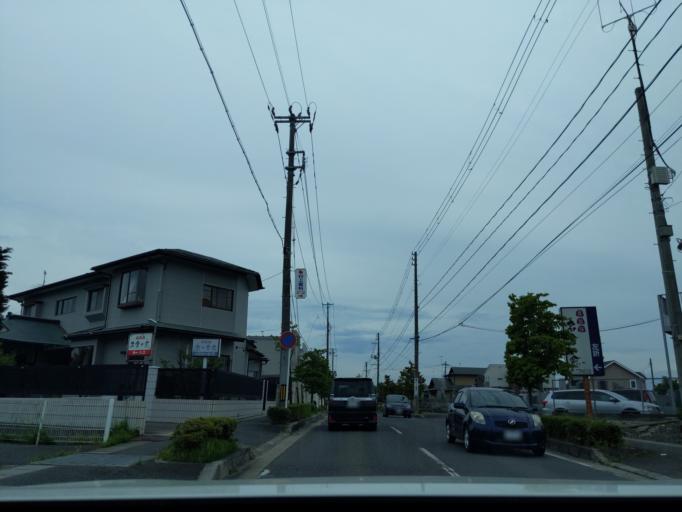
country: JP
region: Fukushima
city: Koriyama
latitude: 37.3736
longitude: 140.3651
